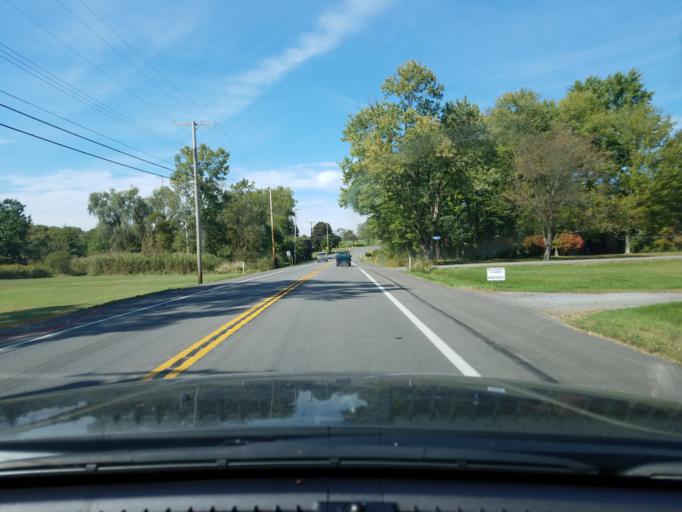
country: US
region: Pennsylvania
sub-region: Lawrence County
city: Ellwood City
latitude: 40.9461
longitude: -80.2839
